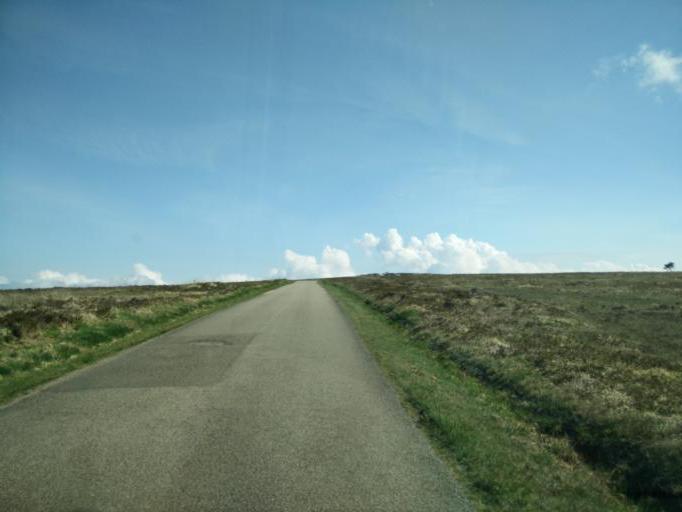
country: FR
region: Brittany
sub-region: Departement du Finistere
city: Plomodiern
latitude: 48.2138
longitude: -4.2412
